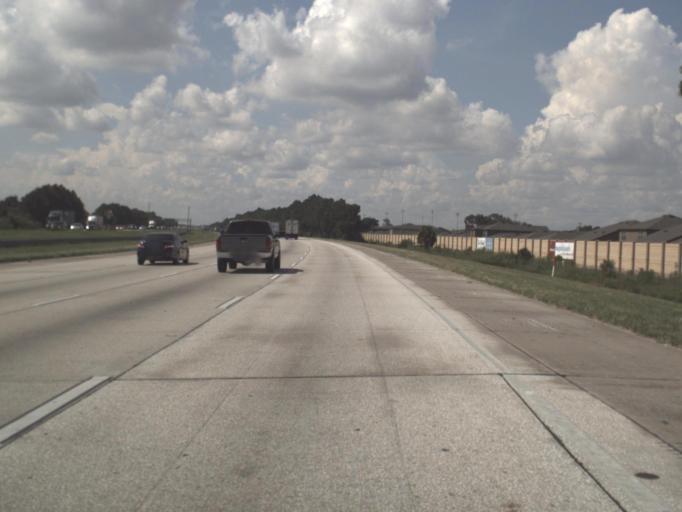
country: US
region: Florida
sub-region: Hillsborough County
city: Progress Village
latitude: 27.8923
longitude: -82.3490
